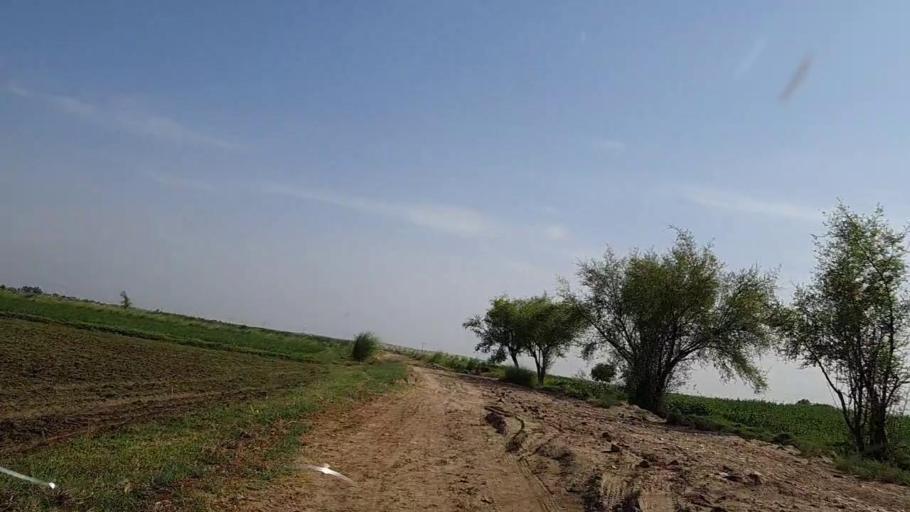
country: PK
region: Sindh
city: Khanpur
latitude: 27.6883
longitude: 69.3677
